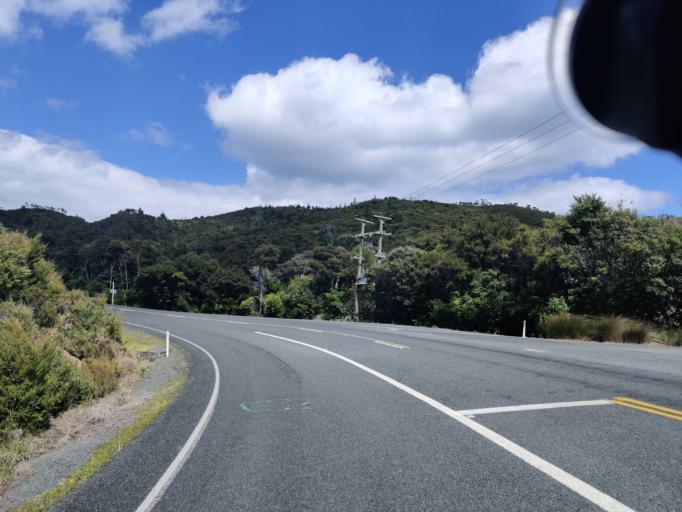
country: NZ
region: Northland
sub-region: Far North District
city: Paihia
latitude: -35.2591
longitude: 174.2254
